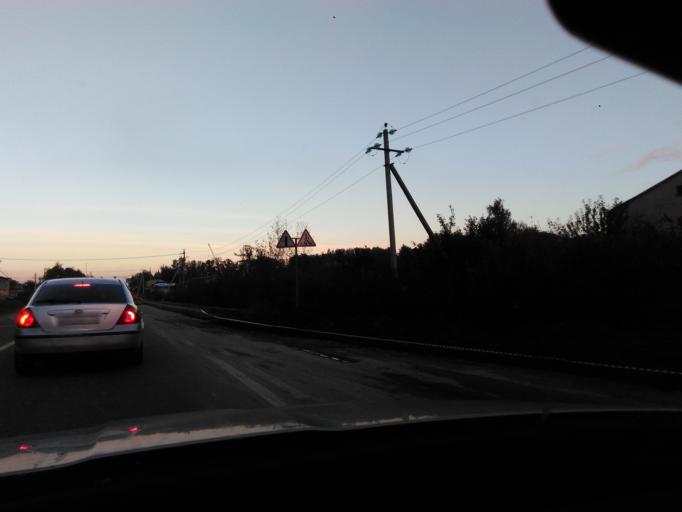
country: RU
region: Moskovskaya
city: Povarovo
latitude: 56.0214
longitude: 37.0032
